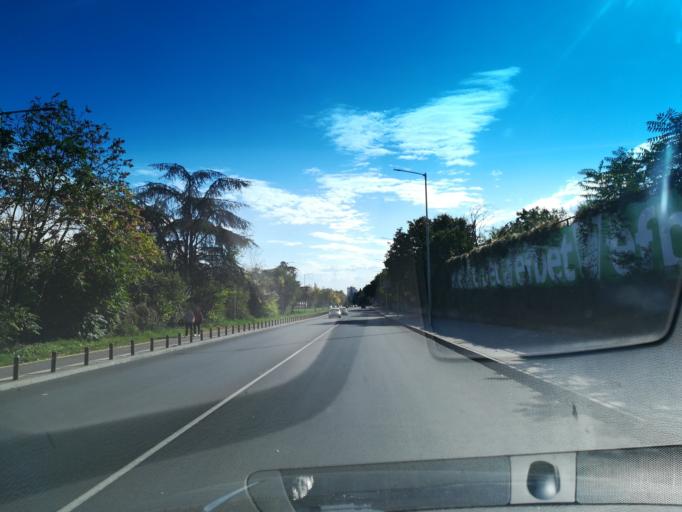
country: BG
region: Stara Zagora
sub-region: Obshtina Stara Zagora
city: Stara Zagora
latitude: 42.4414
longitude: 25.6350
